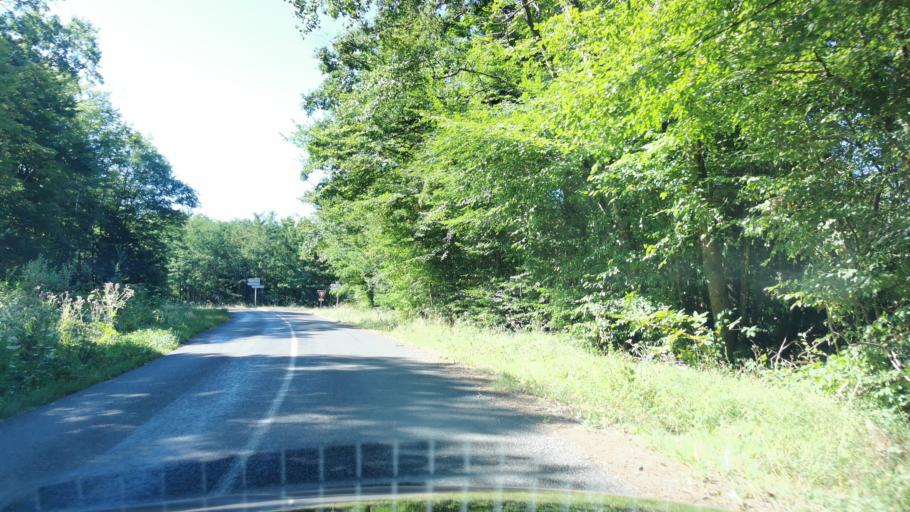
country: FR
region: Bourgogne
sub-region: Departement de Saone-et-Loire
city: Montchanin
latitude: 46.7638
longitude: 4.4722
